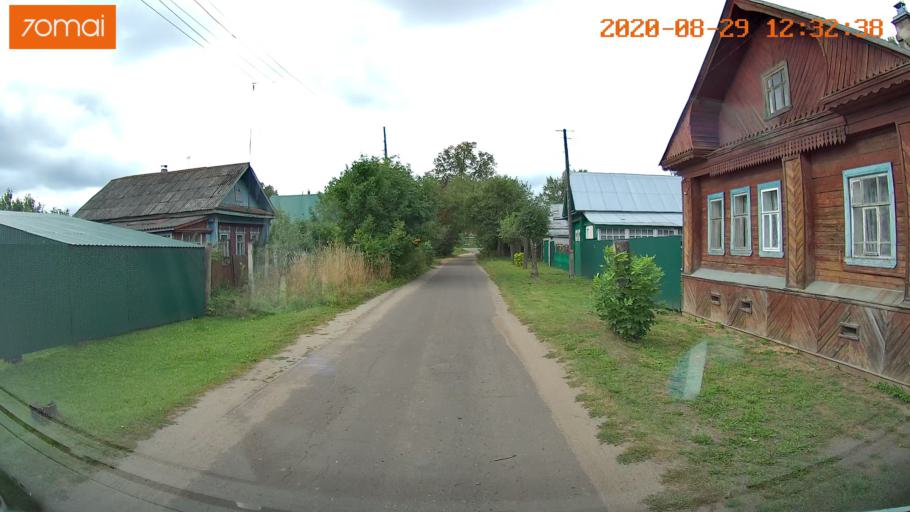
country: RU
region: Ivanovo
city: Yur'yevets
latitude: 57.3137
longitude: 43.0973
